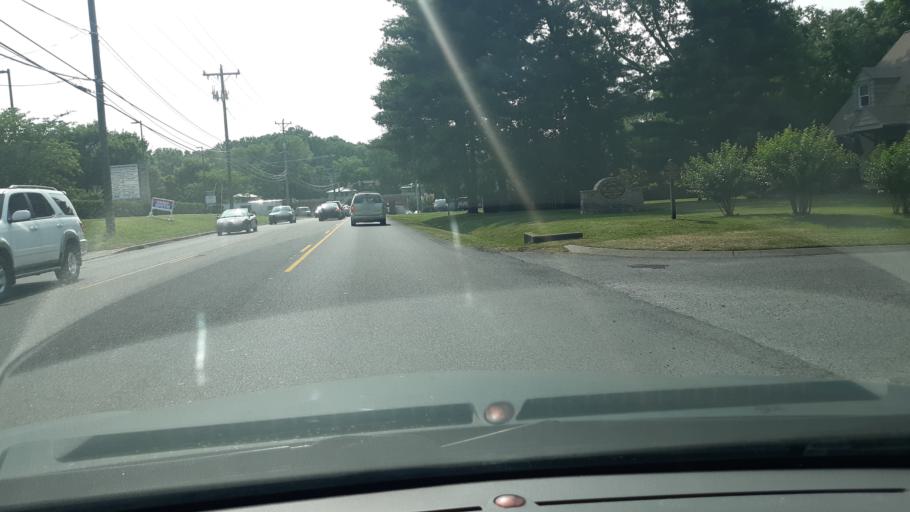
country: US
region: Tennessee
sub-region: Davidson County
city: Lakewood
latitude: 36.1745
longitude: -86.6125
